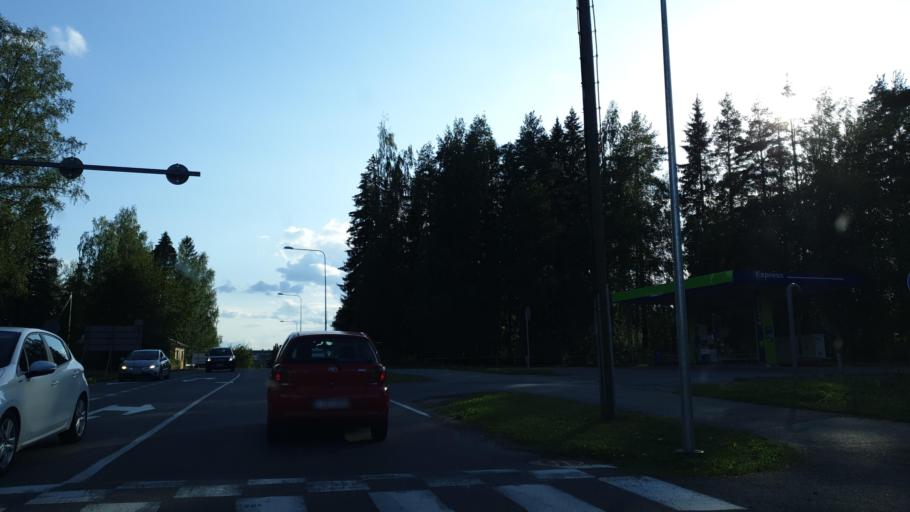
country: FI
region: Northern Savo
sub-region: Varkaus
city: Varkaus
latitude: 62.3354
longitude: 27.8779
